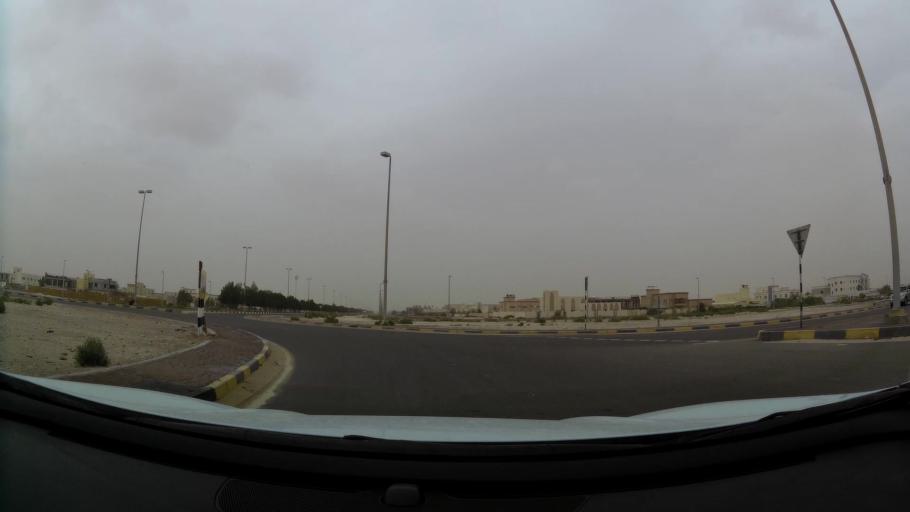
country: AE
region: Abu Dhabi
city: Abu Dhabi
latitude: 24.3919
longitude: 54.7184
